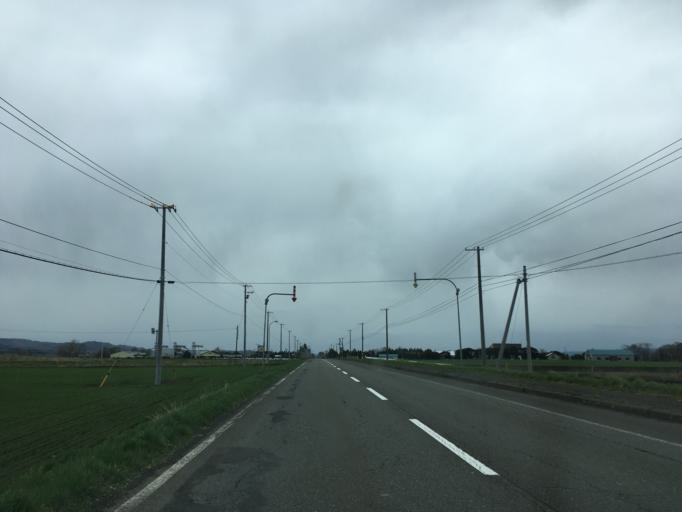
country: JP
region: Hokkaido
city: Chitose
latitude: 42.9271
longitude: 141.8077
